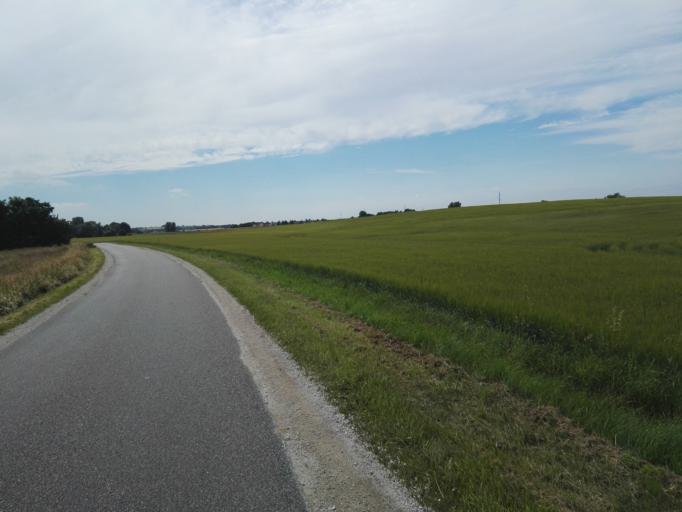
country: DK
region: Capital Region
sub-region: Hillerod Kommune
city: Skaevinge
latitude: 55.8890
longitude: 12.1316
